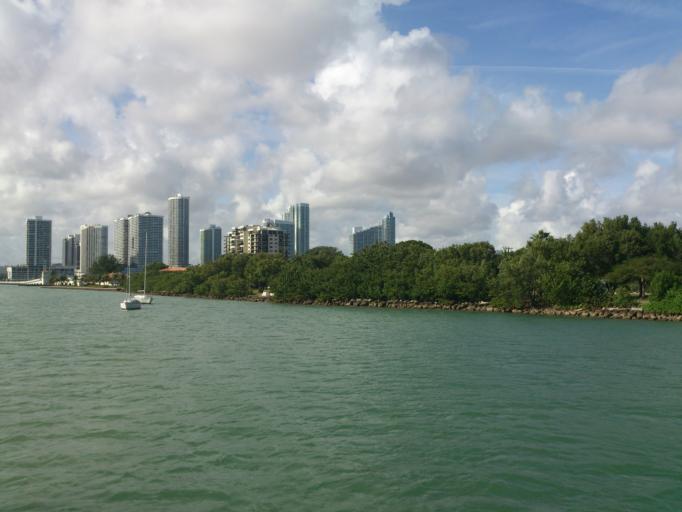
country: US
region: Florida
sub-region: Miami-Dade County
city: Miami
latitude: 25.7891
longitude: -80.1748
